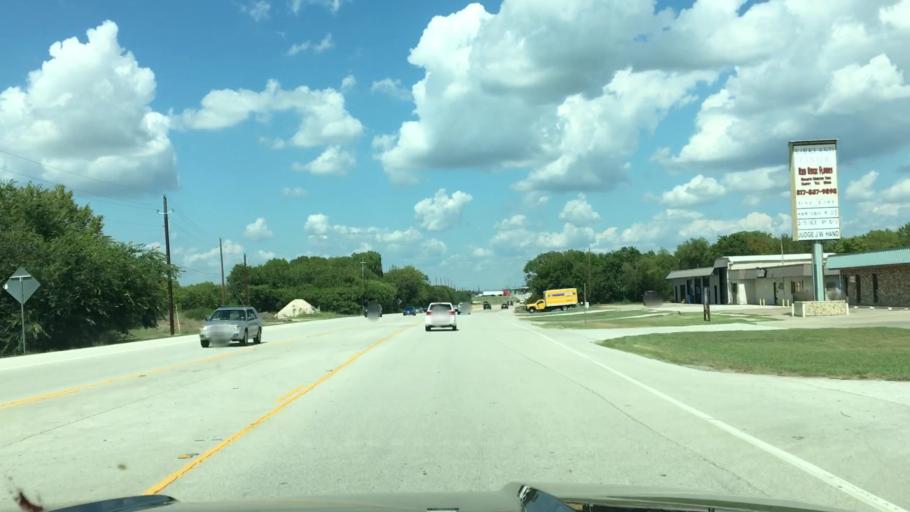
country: US
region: Texas
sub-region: Denton County
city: Roanoke
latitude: 33.0063
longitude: -97.2263
